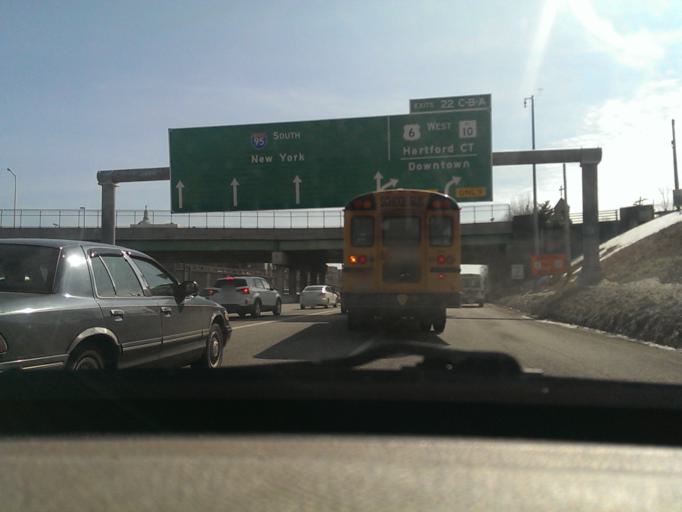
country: US
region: Rhode Island
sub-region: Providence County
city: Providence
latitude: 41.8355
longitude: -71.4160
